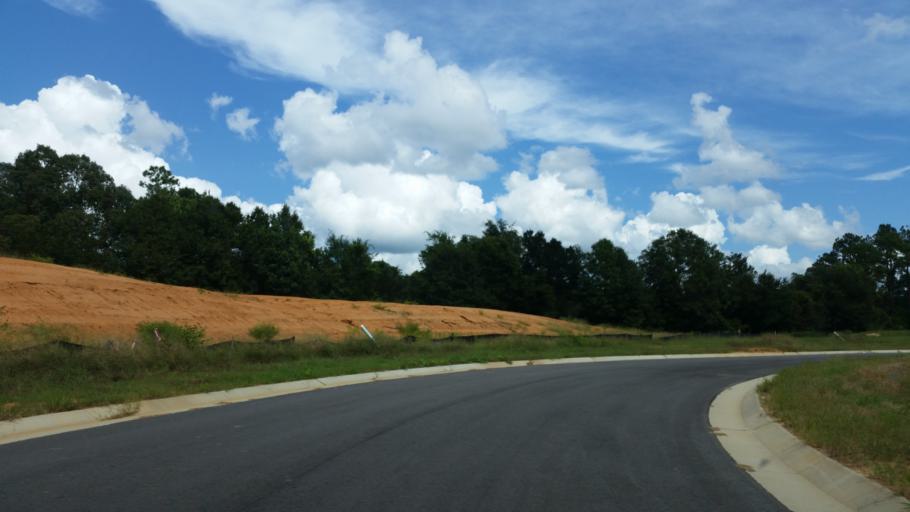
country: US
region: Florida
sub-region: Escambia County
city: Cantonment
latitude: 30.5392
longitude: -87.4074
